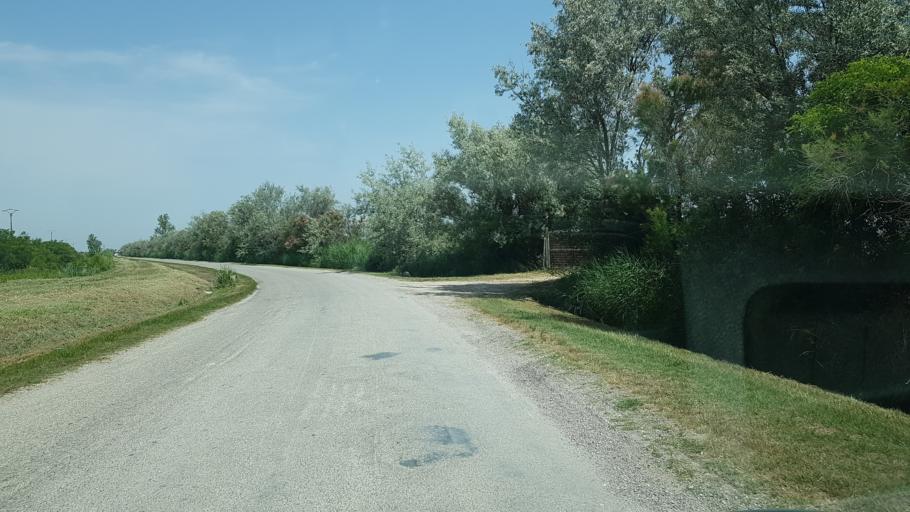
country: FR
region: Languedoc-Roussillon
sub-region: Departement du Gard
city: Saint-Gilles
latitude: 43.5741
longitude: 4.5044
